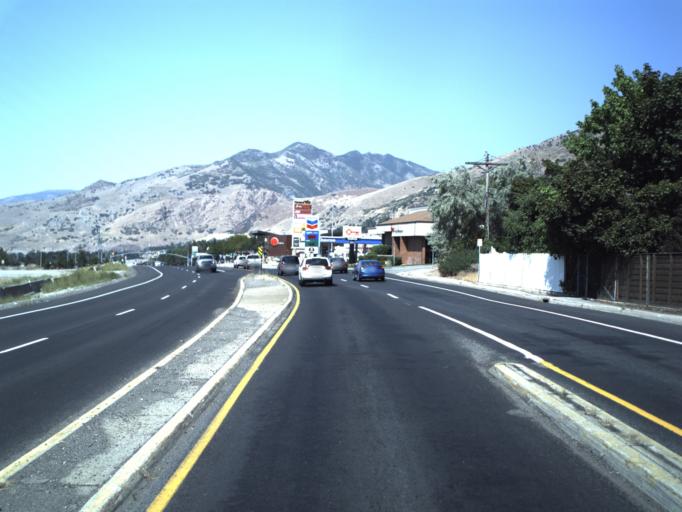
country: US
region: Utah
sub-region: Salt Lake County
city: Mount Olympus
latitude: 40.6830
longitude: -111.7962
